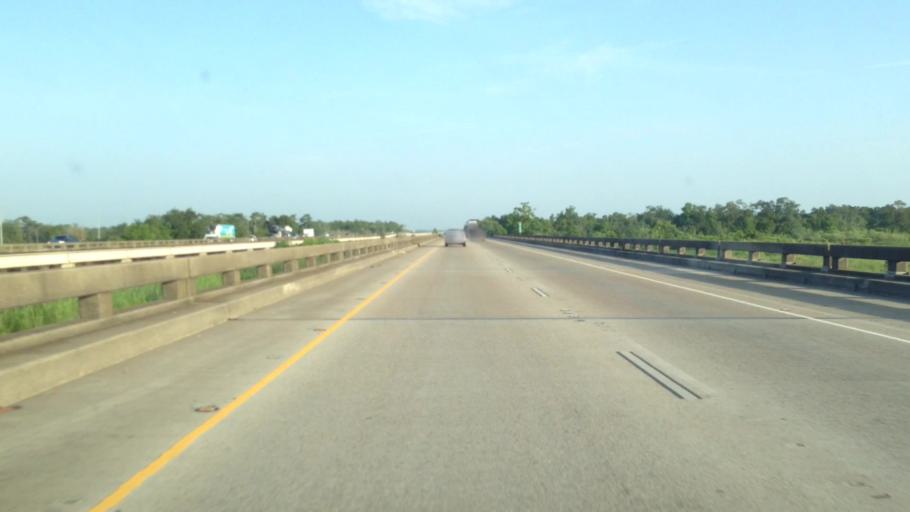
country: US
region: Louisiana
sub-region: Saint Charles Parish
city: Norco
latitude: 30.0511
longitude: -90.3647
